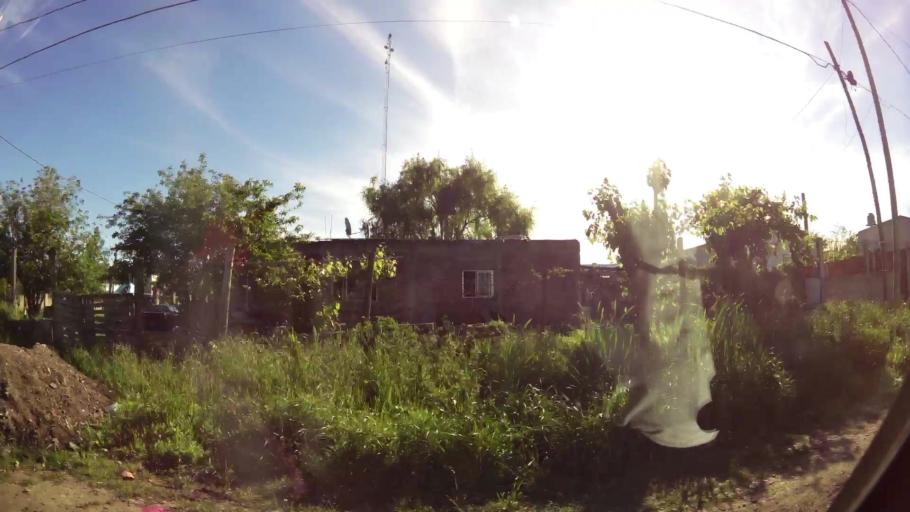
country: AR
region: Buenos Aires
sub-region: Partido de Almirante Brown
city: Adrogue
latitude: -34.8266
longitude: -58.3567
